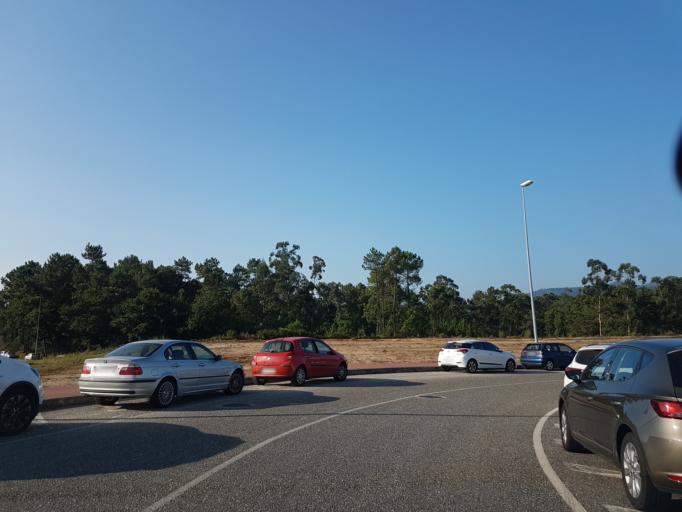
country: ES
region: Galicia
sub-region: Provincia de Pontevedra
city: Porrino
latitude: 42.1891
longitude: -8.6230
